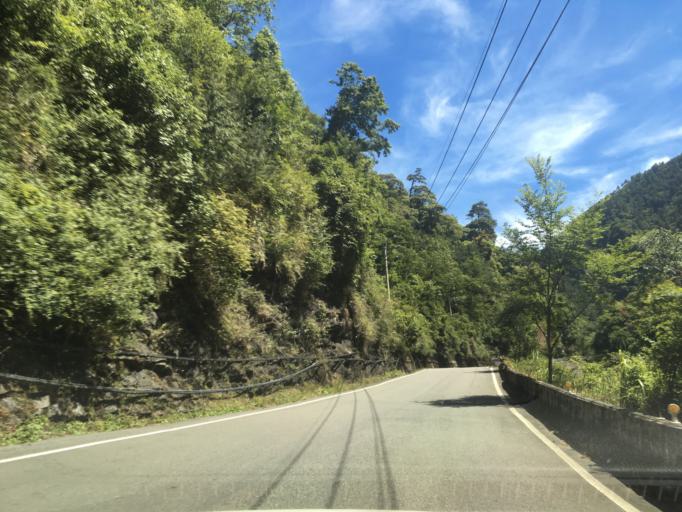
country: TW
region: Taiwan
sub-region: Nantou
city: Puli
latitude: 24.2182
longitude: 121.2643
